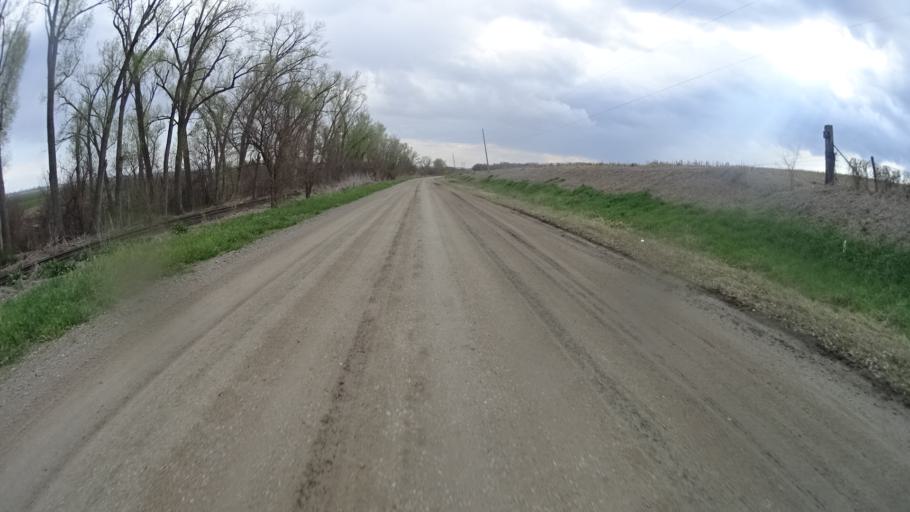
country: US
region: Nebraska
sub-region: Sarpy County
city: Offutt Air Force Base
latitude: 41.0953
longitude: -95.9135
